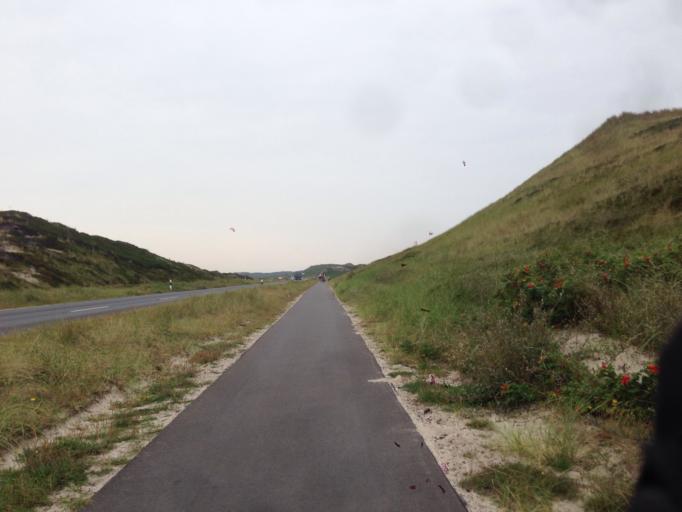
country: DE
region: Schleswig-Holstein
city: Westerland
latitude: 54.8133
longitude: 8.2900
